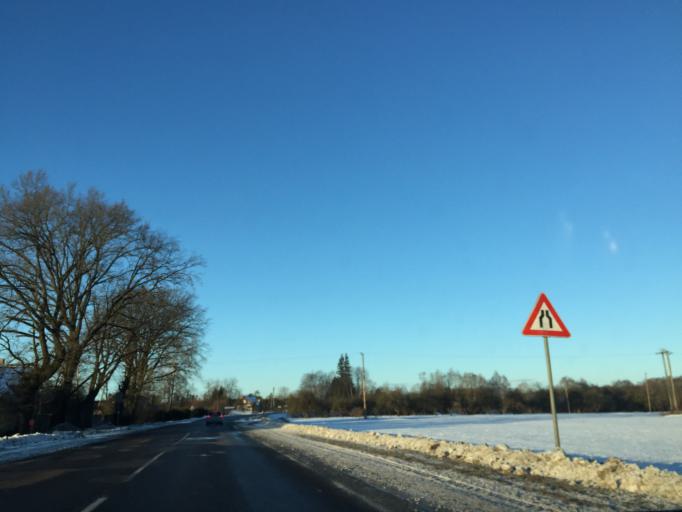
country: LV
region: Kegums
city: Kegums
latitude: 56.7450
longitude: 24.6701
